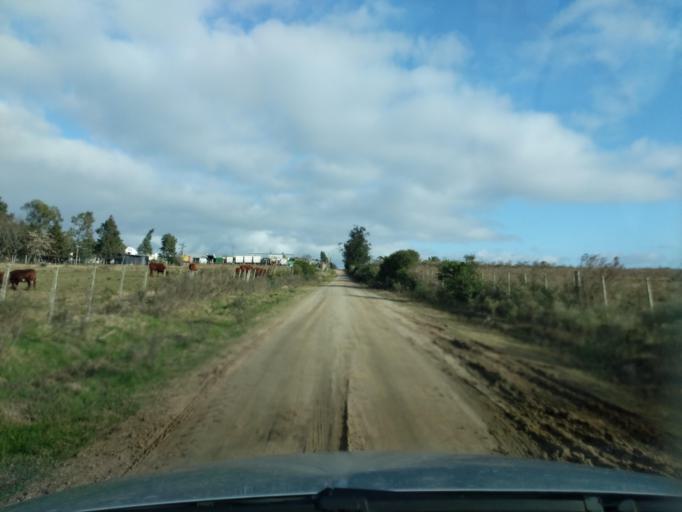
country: UY
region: Florida
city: Florida
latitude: -34.0787
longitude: -56.2177
